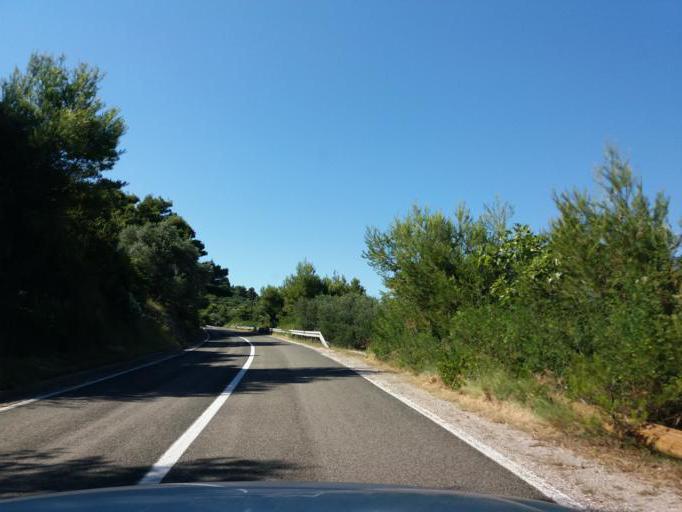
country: HR
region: Zadarska
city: Ugljan
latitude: 44.1140
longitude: 14.9231
